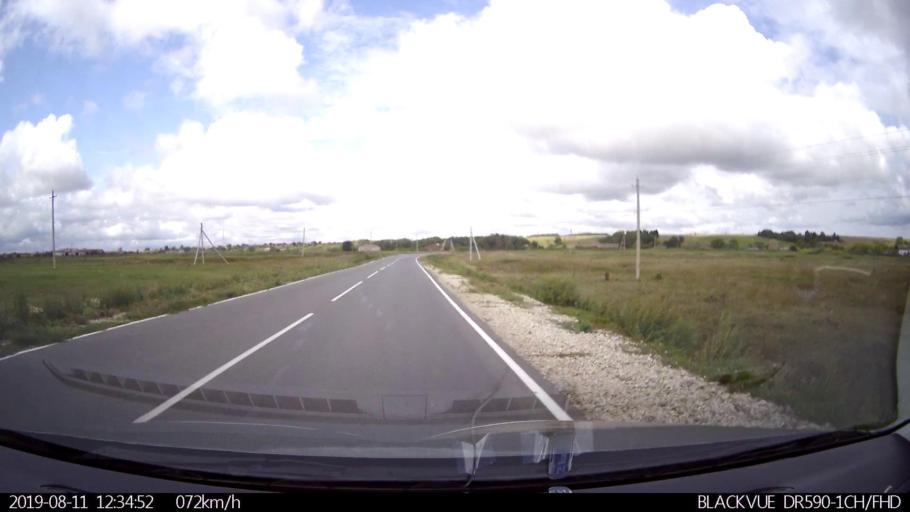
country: RU
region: Ulyanovsk
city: Ignatovka
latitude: 53.8202
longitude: 47.8371
